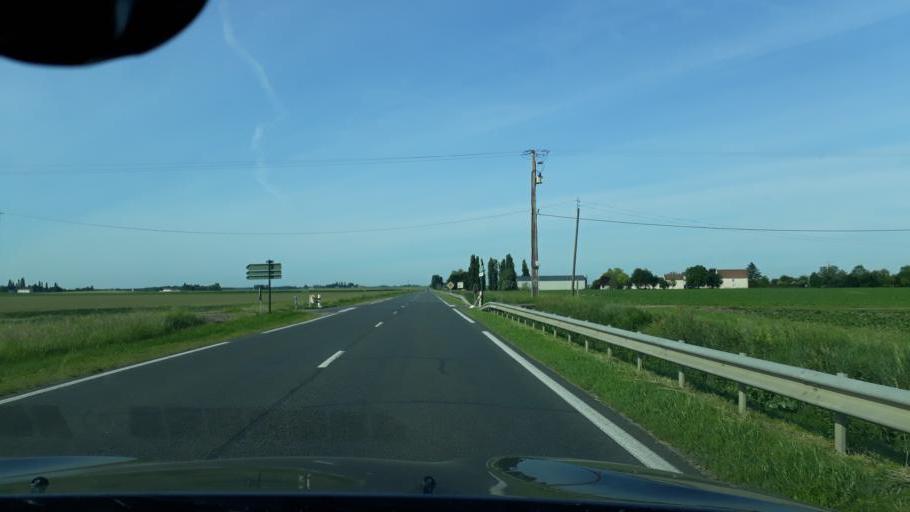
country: FR
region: Centre
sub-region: Departement du Loiret
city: Chilleurs-aux-Bois
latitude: 48.1086
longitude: 2.1742
